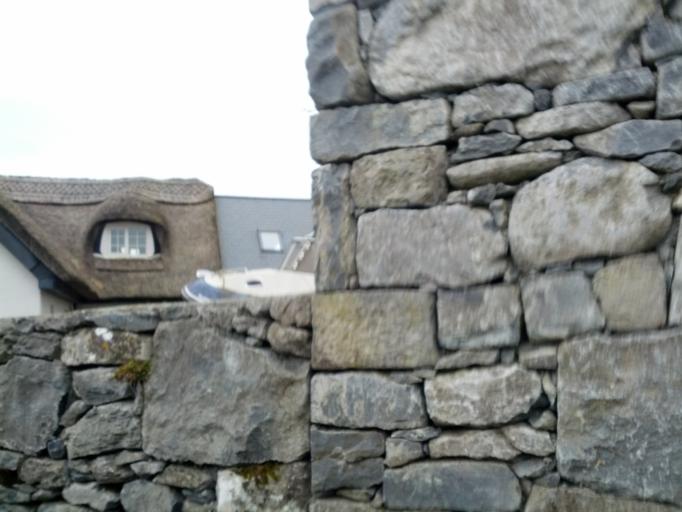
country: IE
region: Connaught
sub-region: County Galway
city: Oranmore
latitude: 53.1945
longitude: -8.9302
